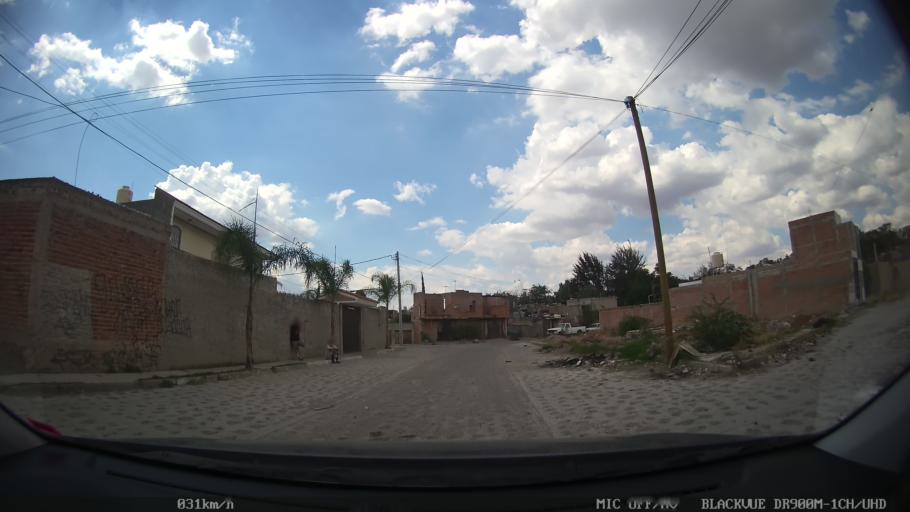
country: MX
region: Jalisco
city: Tlaquepaque
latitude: 20.6804
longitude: -103.2662
